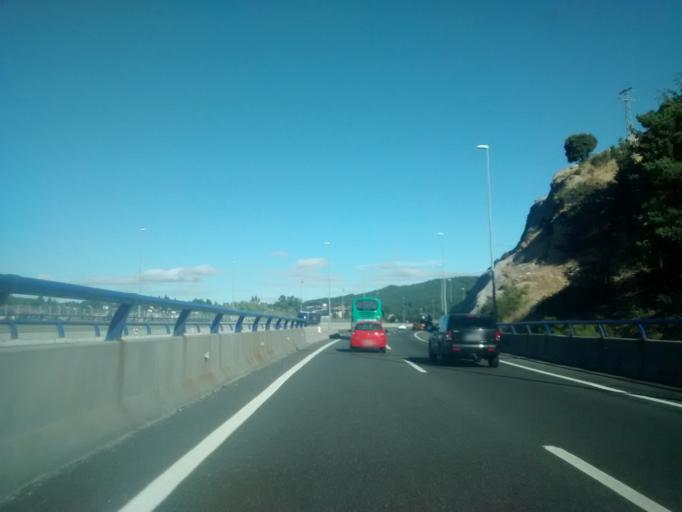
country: ES
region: Castille and Leon
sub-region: Provincia de Avila
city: Peguerinos
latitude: 40.7151
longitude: -4.1840
